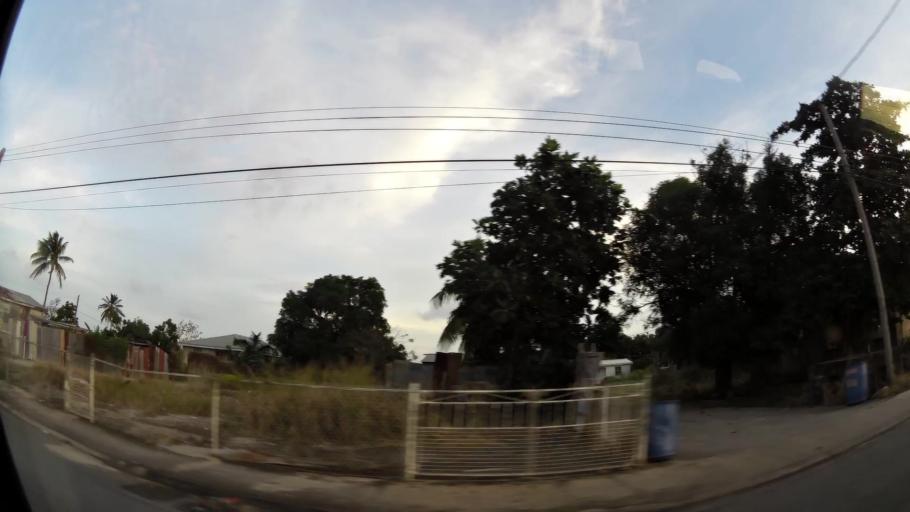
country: BB
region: Saint Philip
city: Crane
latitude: 13.1027
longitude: -59.4929
